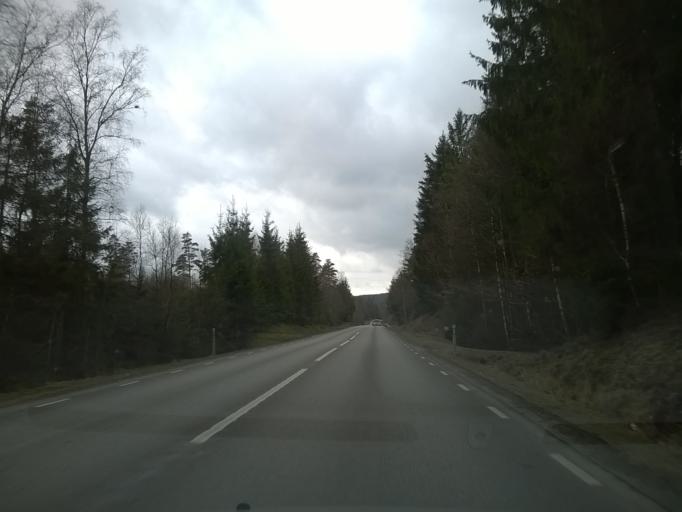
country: SE
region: Halland
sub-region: Varbergs Kommun
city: Tvaaker
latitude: 57.1525
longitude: 12.6342
